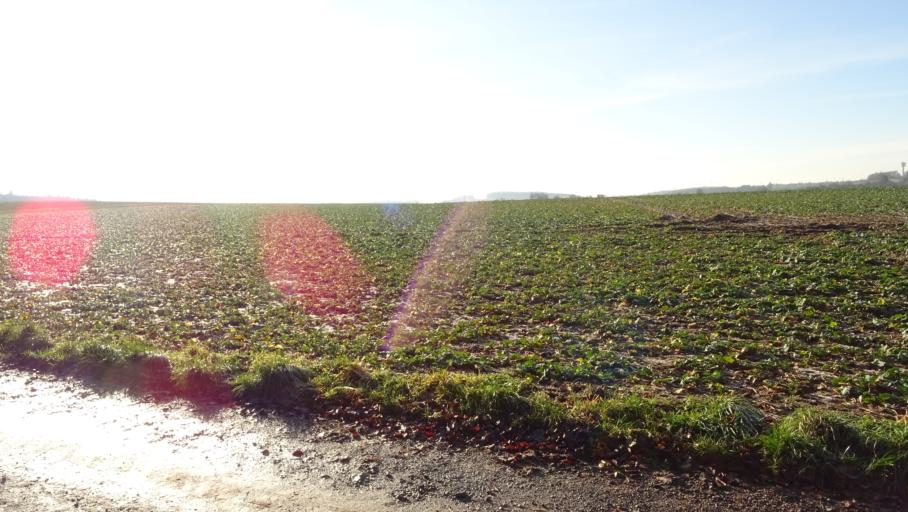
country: DE
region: Baden-Wuerttemberg
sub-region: Karlsruhe Region
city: Mosbach
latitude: 49.3478
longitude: 9.1950
